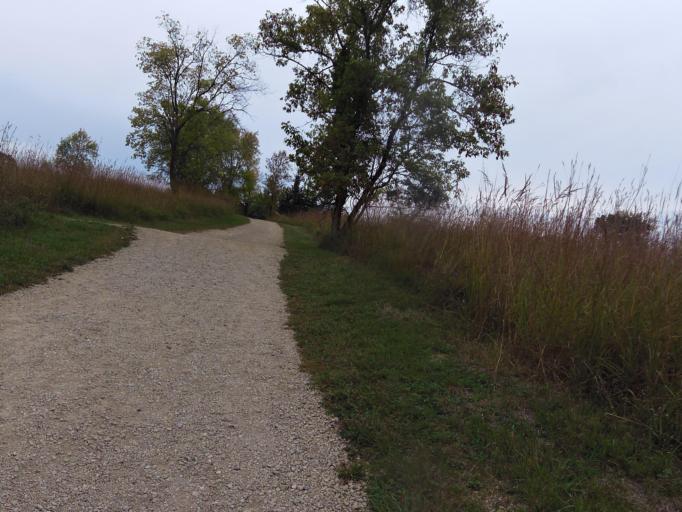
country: US
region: Minnesota
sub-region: Washington County
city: Afton
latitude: 44.8646
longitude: -92.7781
